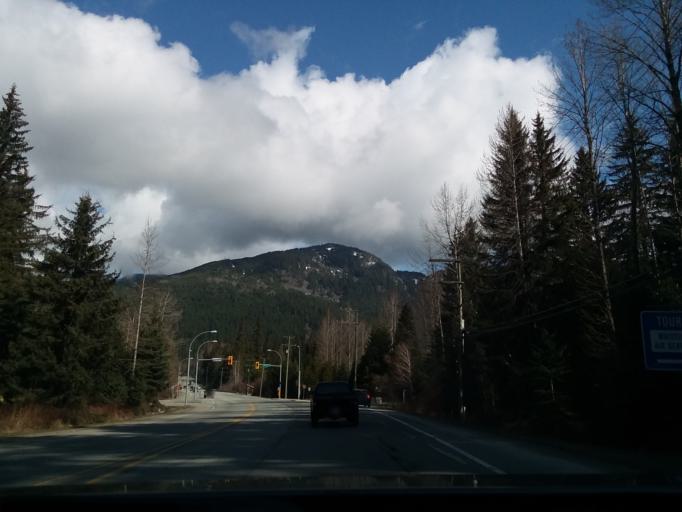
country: CA
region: British Columbia
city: Whistler
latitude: 50.1417
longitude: -122.9567
